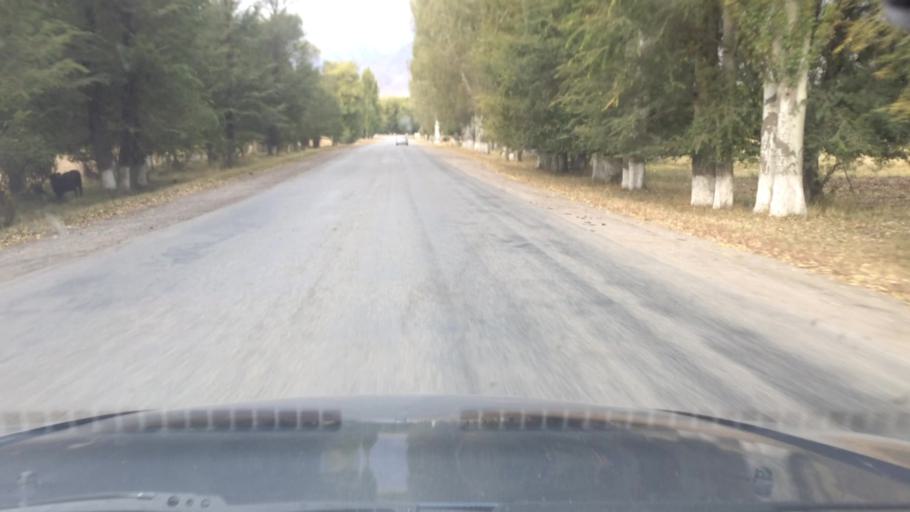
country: KG
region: Ysyk-Koel
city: Tyup
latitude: 42.7859
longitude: 78.2680
